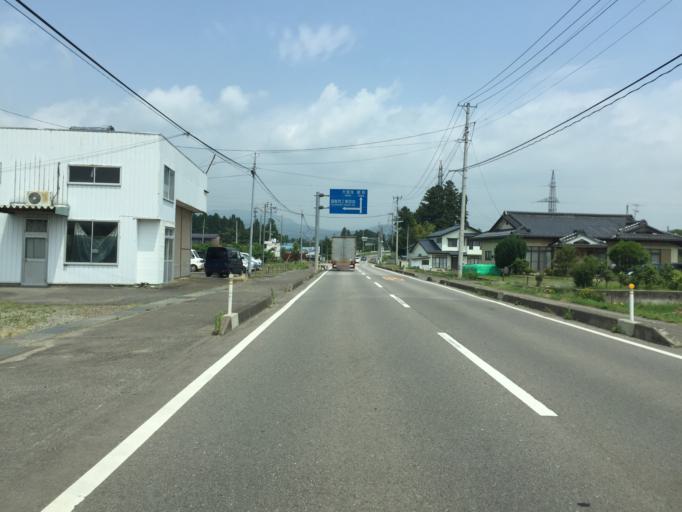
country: JP
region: Fukushima
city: Fukushima-shi
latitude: 37.7524
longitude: 140.4018
